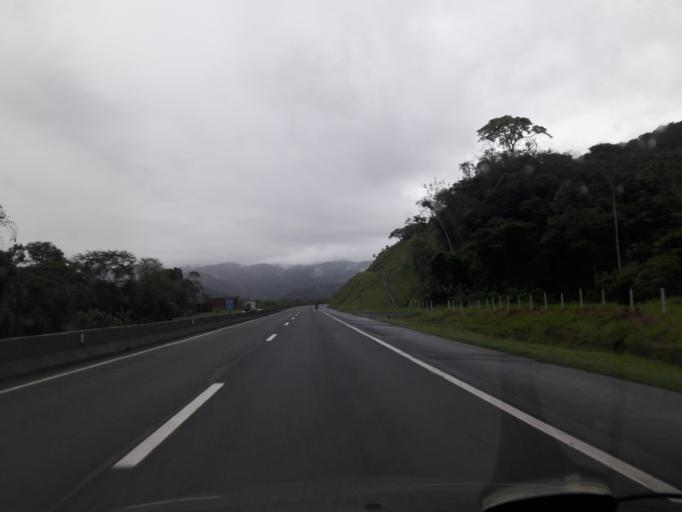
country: BR
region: Sao Paulo
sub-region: Miracatu
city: Miracatu
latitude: -24.2112
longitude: -47.3702
